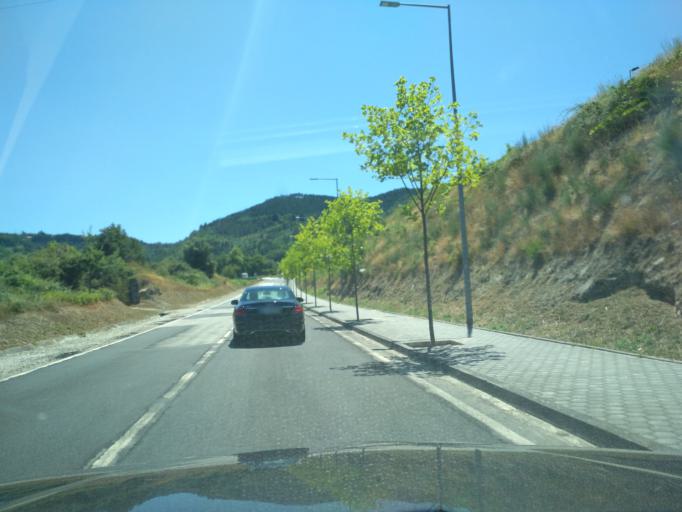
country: PT
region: Vila Real
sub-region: Ribeira de Pena
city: Sobreira
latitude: 41.5233
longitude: -7.7911
